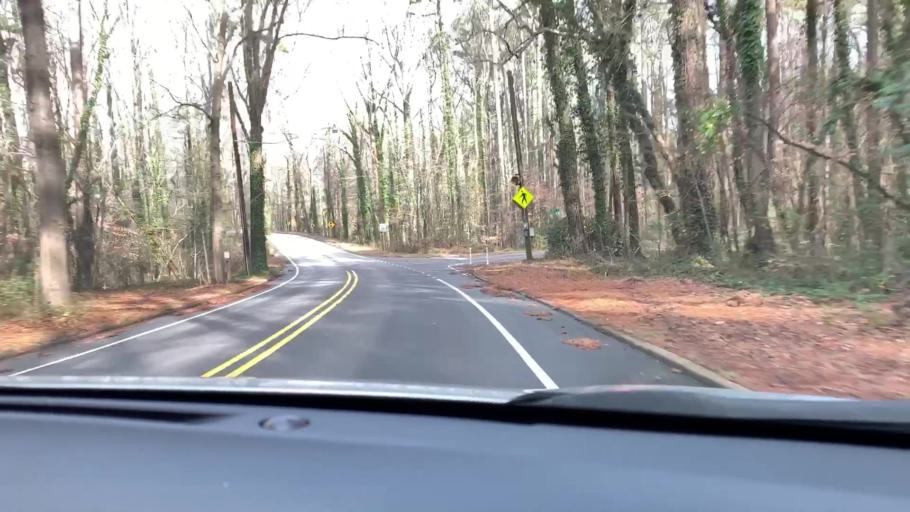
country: US
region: North Carolina
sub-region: Durham County
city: Durham
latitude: 35.9892
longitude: -78.9398
